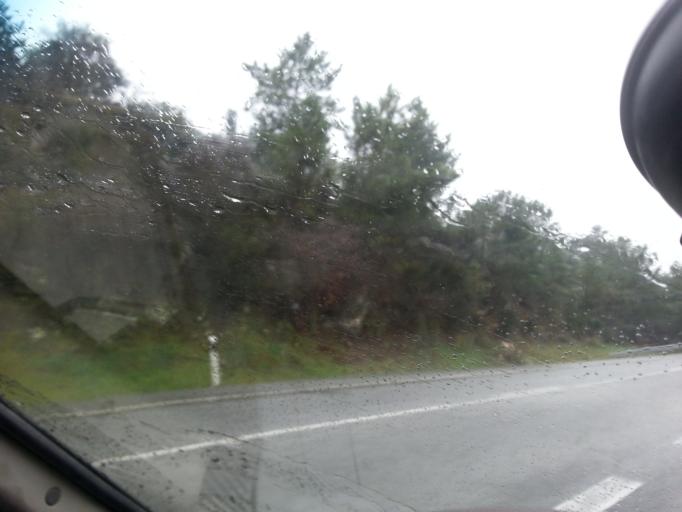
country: PT
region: Guarda
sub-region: Fornos de Algodres
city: Fornos de Algodres
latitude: 40.6158
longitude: -7.6039
